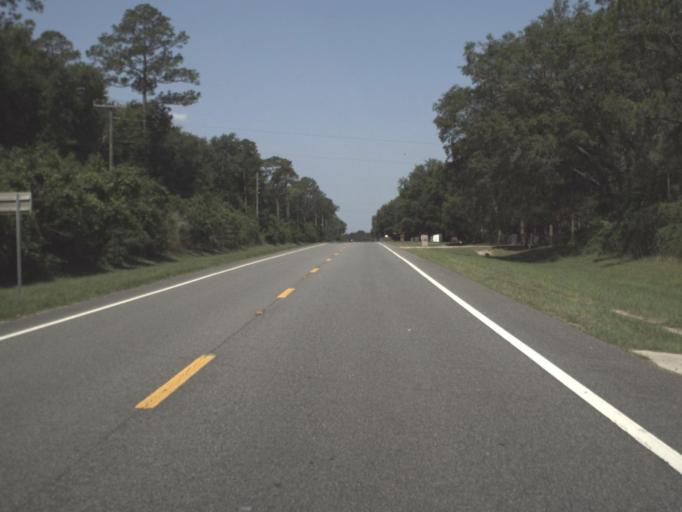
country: US
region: Florida
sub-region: Clay County
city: Asbury Lake
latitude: 29.9823
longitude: -81.8323
